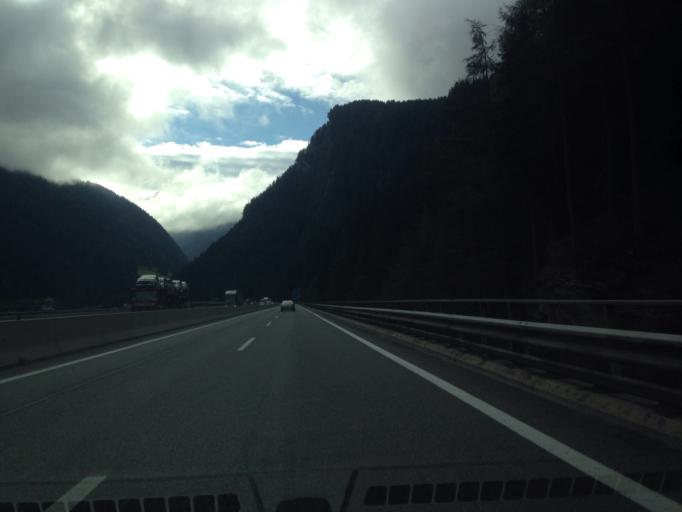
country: AT
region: Tyrol
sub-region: Politischer Bezirk Innsbruck Land
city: Gries am Brenner
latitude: 47.0301
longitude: 11.4872
